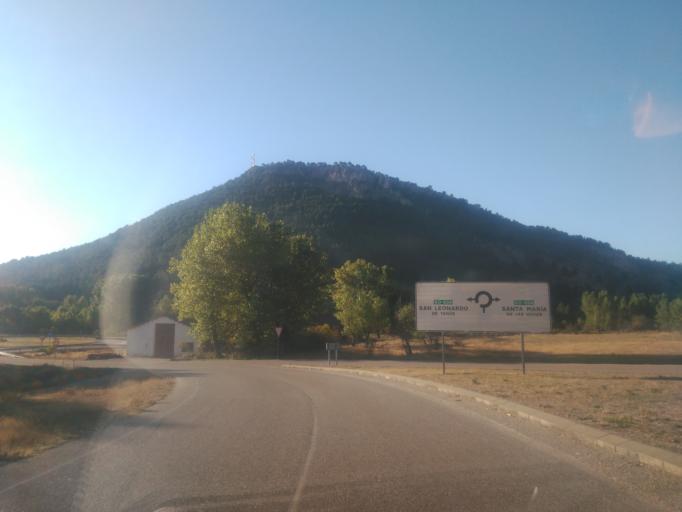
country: ES
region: Castille and Leon
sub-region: Provincia de Soria
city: San Leonardo de Yague
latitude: 41.8250
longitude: -3.0821
